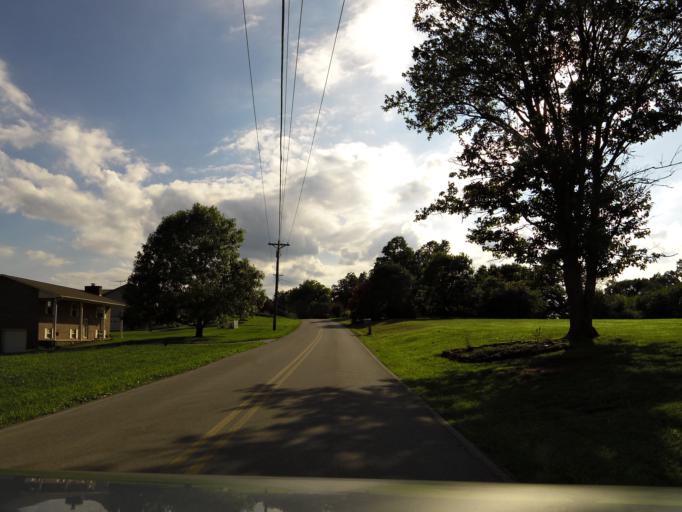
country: US
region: Tennessee
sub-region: Loudon County
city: Greenback
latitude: 35.6617
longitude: -84.0883
